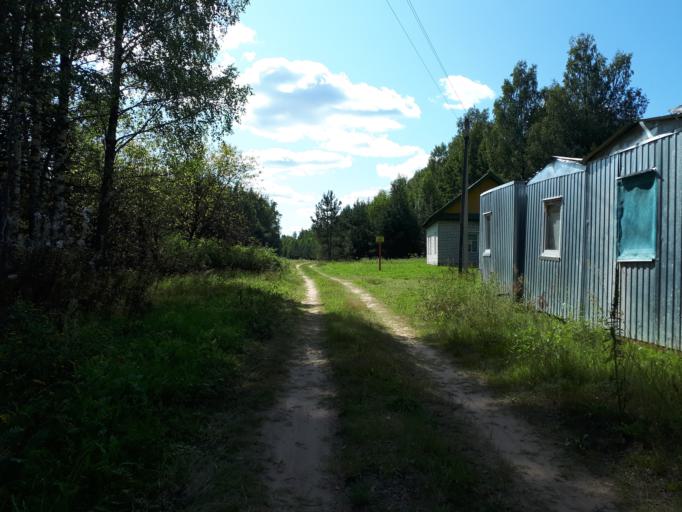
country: BY
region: Vitebsk
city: Rasony
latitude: 55.9884
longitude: 28.5976
